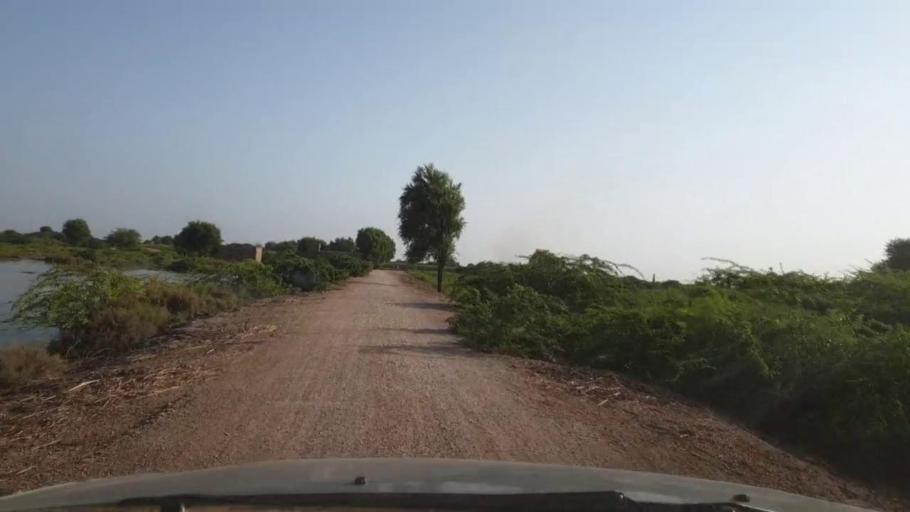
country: PK
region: Sindh
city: Tando Ghulam Ali
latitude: 25.1181
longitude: 68.9407
